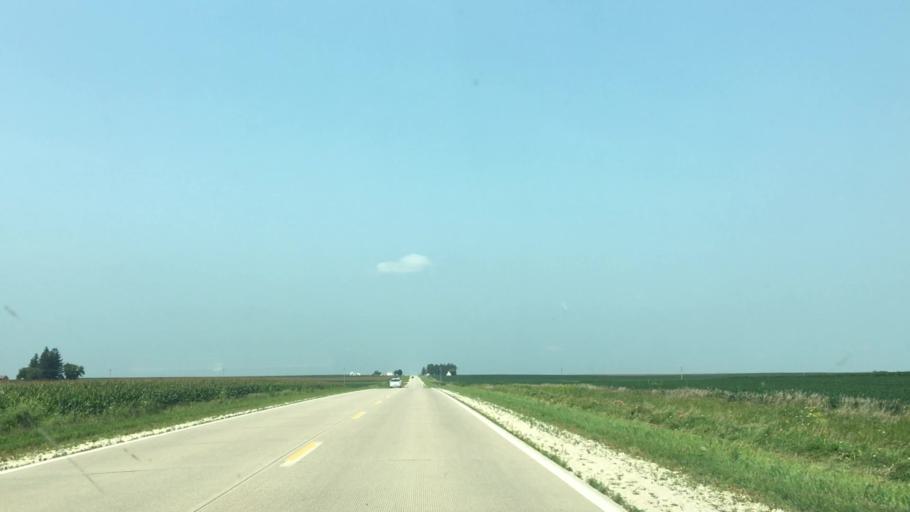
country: US
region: Iowa
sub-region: Fayette County
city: Oelwein
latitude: 42.6970
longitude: -91.8050
